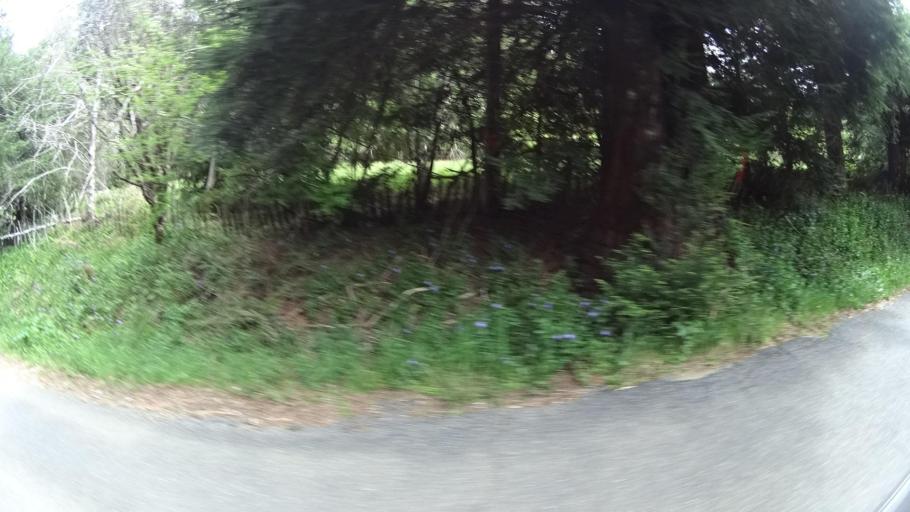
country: US
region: California
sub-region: Humboldt County
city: Redway
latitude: 40.0041
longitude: -123.9286
